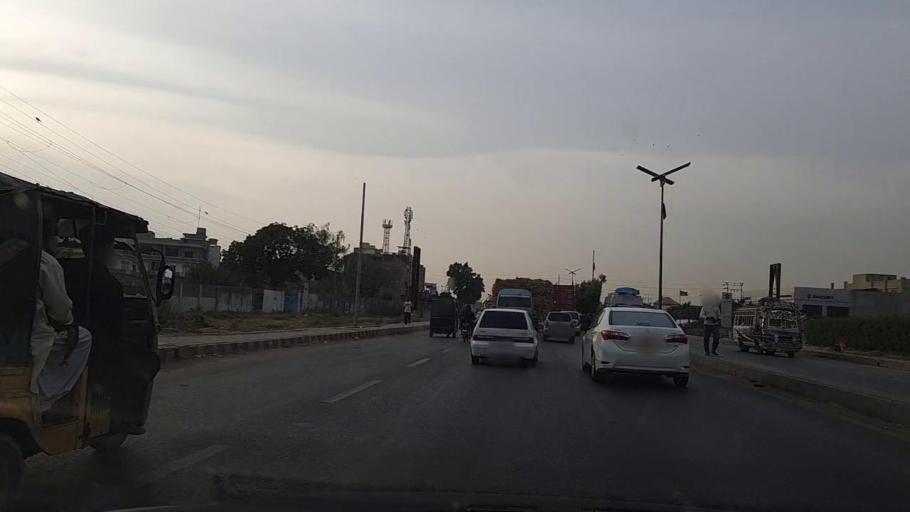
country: PK
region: Sindh
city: Malir Cantonment
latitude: 24.8536
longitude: 67.2460
